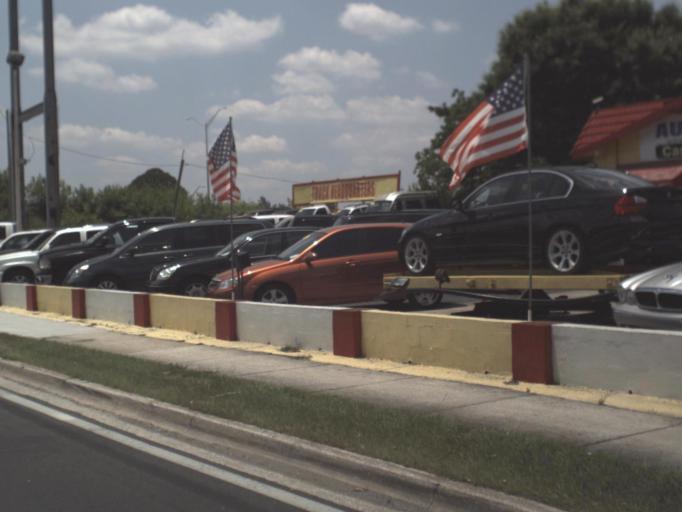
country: US
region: Florida
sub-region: Duval County
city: Jacksonville
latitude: 30.3183
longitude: -81.7308
